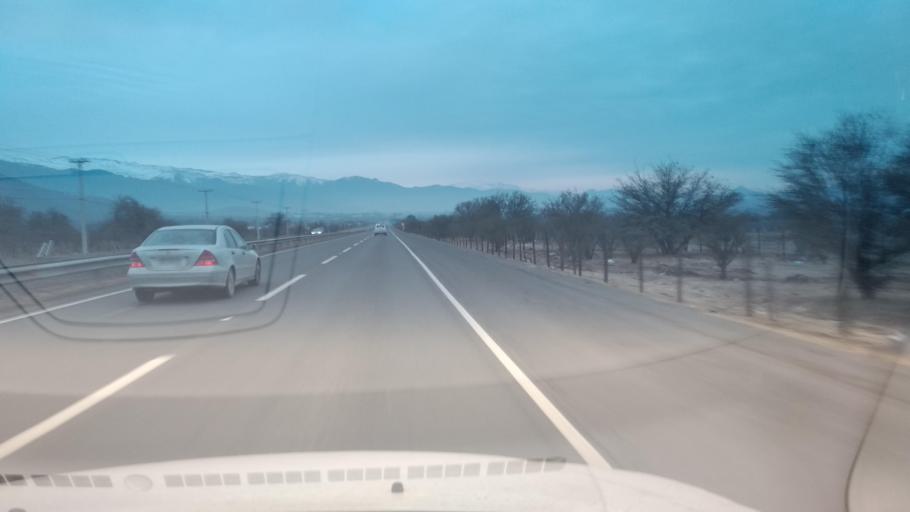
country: CL
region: Santiago Metropolitan
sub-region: Provincia de Chacabuco
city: Chicureo Abajo
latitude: -33.1148
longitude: -70.6842
